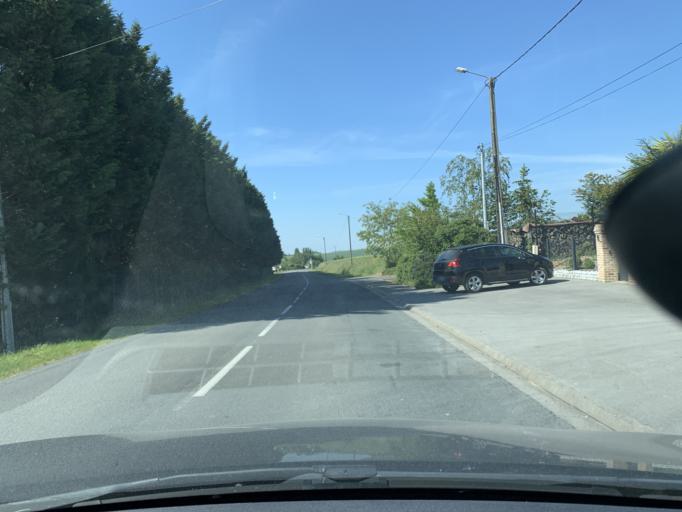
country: FR
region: Nord-Pas-de-Calais
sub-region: Departement du Nord
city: Masnieres
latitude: 50.0892
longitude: 3.2261
